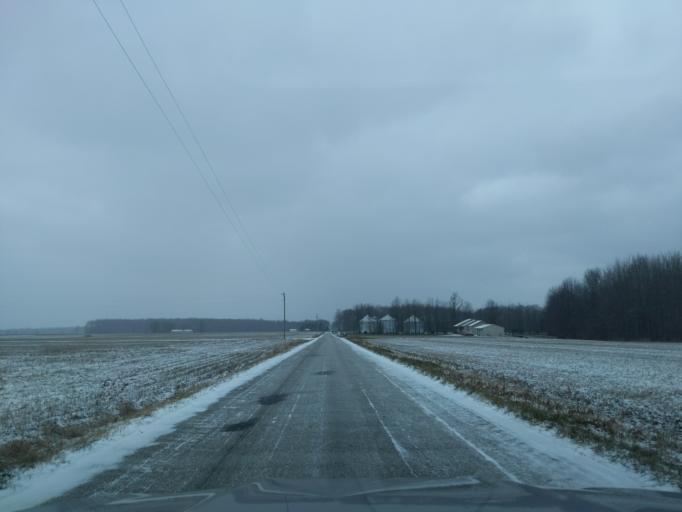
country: US
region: Indiana
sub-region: Decatur County
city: Greensburg
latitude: 39.2340
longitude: -85.4711
